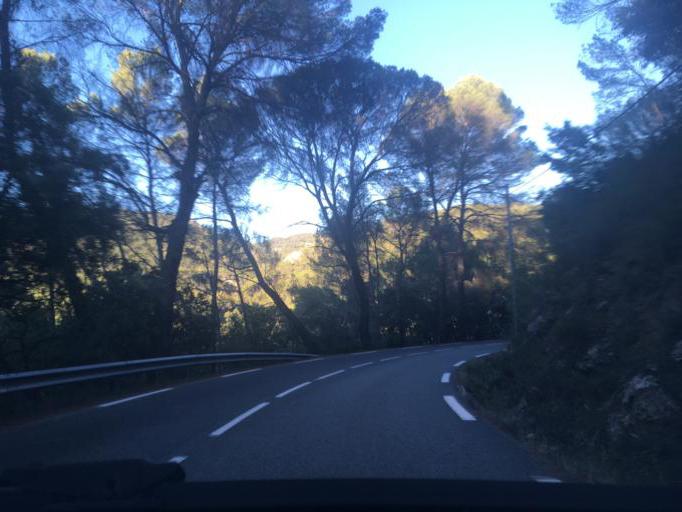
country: FR
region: Provence-Alpes-Cote d'Azur
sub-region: Departement du Var
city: Flayosc
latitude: 43.5638
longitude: 6.4185
